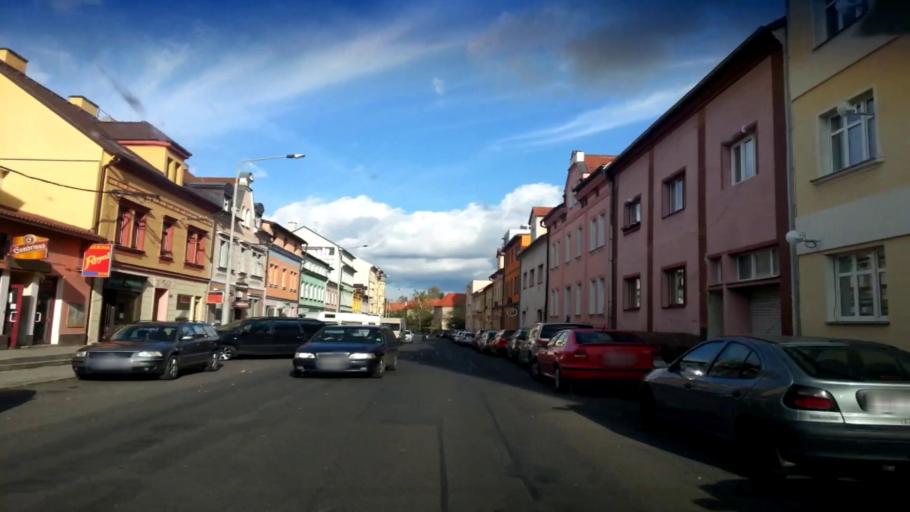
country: CZ
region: Karlovarsky
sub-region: Okres Cheb
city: Cheb
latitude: 50.0679
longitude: 12.3729
